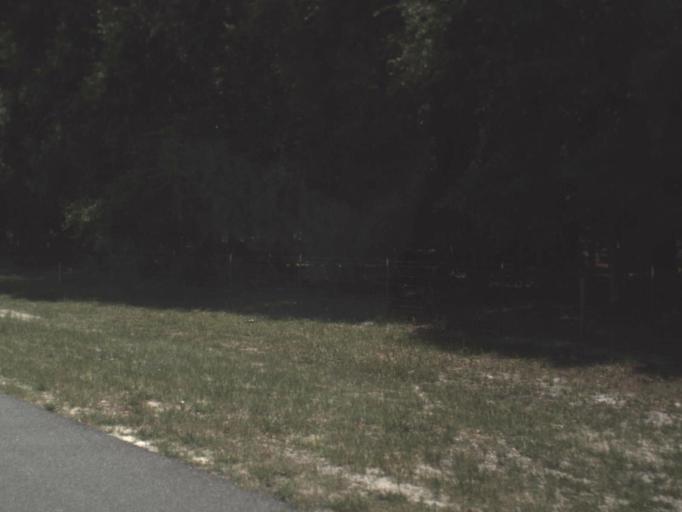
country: US
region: Florida
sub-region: Dixie County
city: Cross City
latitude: 29.6612
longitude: -82.9841
